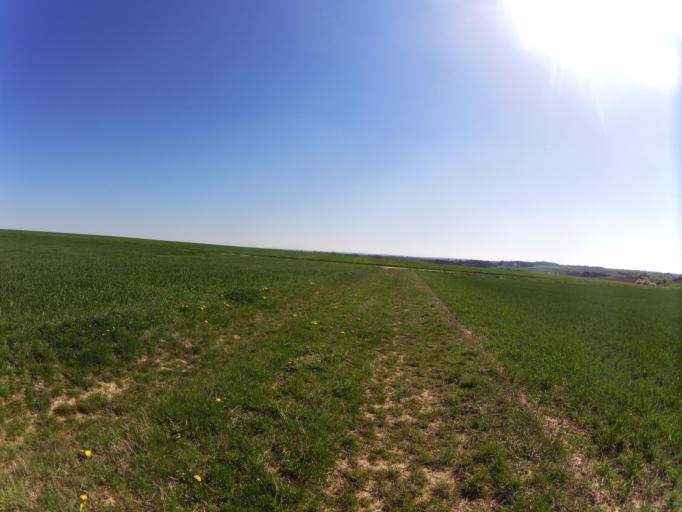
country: DE
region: Bavaria
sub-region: Regierungsbezirk Unterfranken
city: Winterhausen
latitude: 49.6821
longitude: 10.0036
